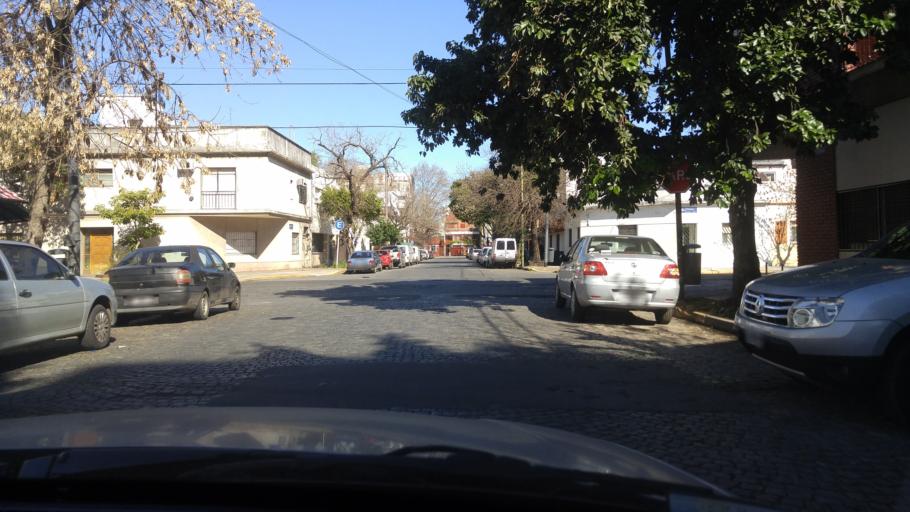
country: AR
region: Buenos Aires F.D.
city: Villa Santa Rita
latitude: -34.6241
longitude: -58.4868
